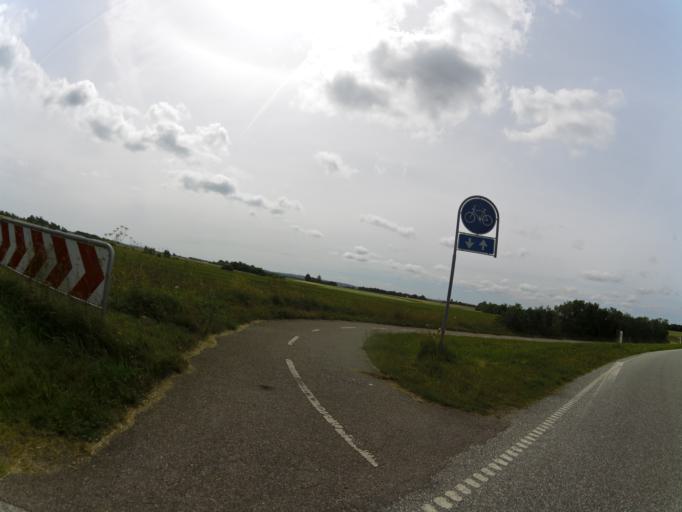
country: DK
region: North Denmark
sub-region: Bronderslev Kommune
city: Dronninglund
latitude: 57.2691
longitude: 10.3440
